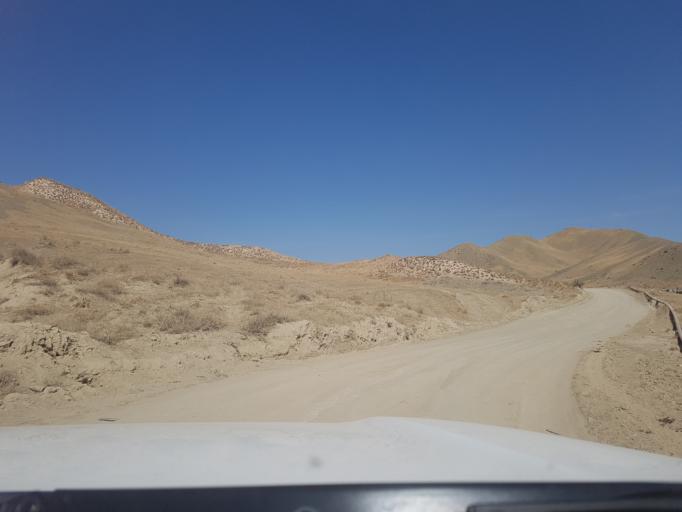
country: TM
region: Ahal
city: Baharly
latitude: 38.2530
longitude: 56.8902
